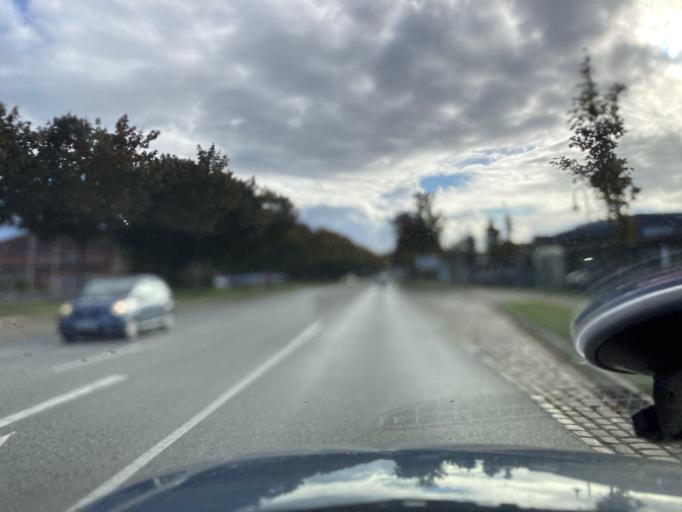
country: DE
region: Schleswig-Holstein
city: Budelsdorf
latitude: 54.3227
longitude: 9.6932
